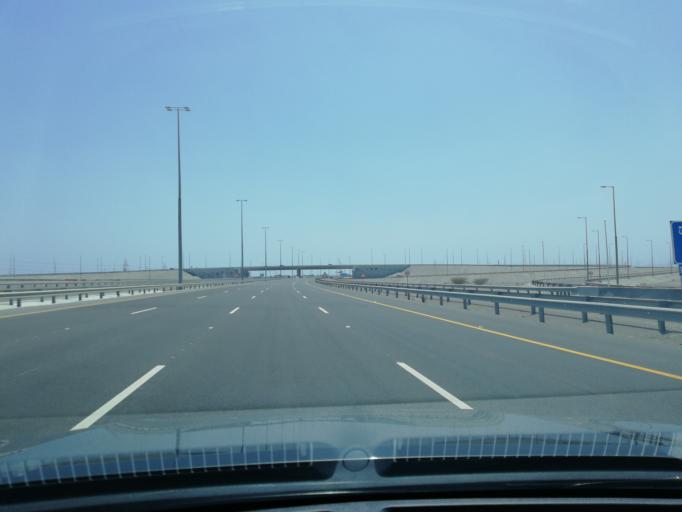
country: OM
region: Al Batinah
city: Barka'
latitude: 23.6331
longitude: 57.8685
